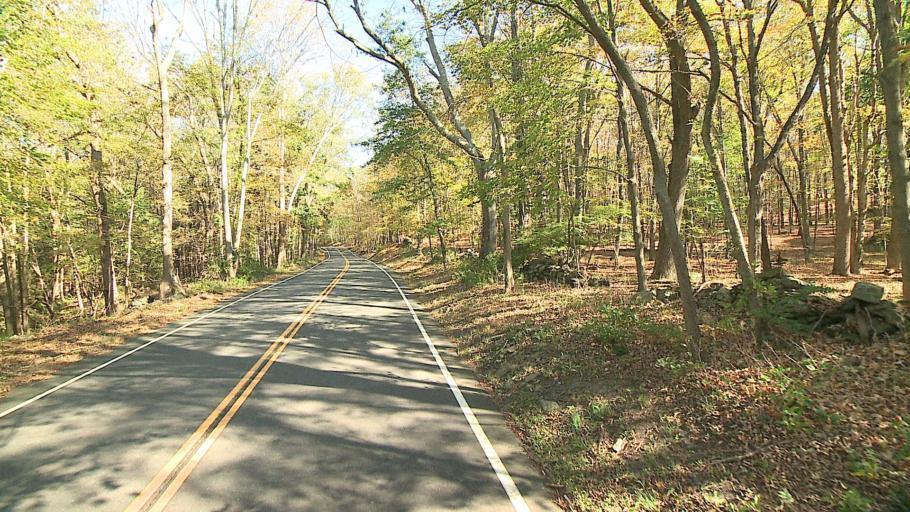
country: US
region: Connecticut
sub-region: Fairfield County
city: Westport
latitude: 41.2326
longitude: -73.3150
